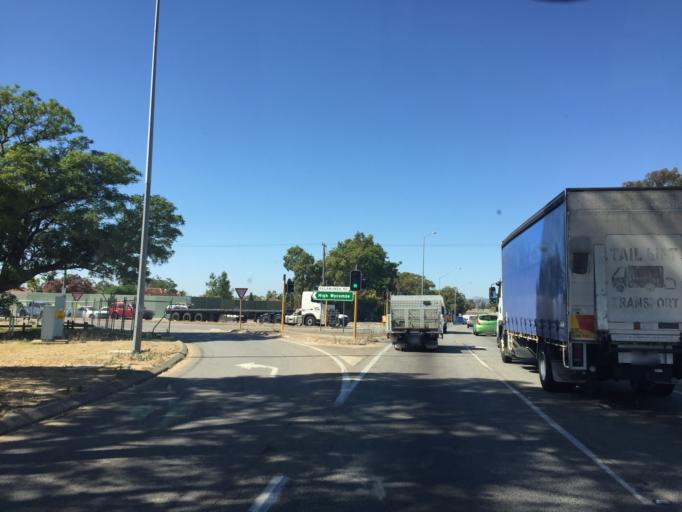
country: AU
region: Western Australia
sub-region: Kalamunda
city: Maida Vale
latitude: -31.9410
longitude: 116.0158
